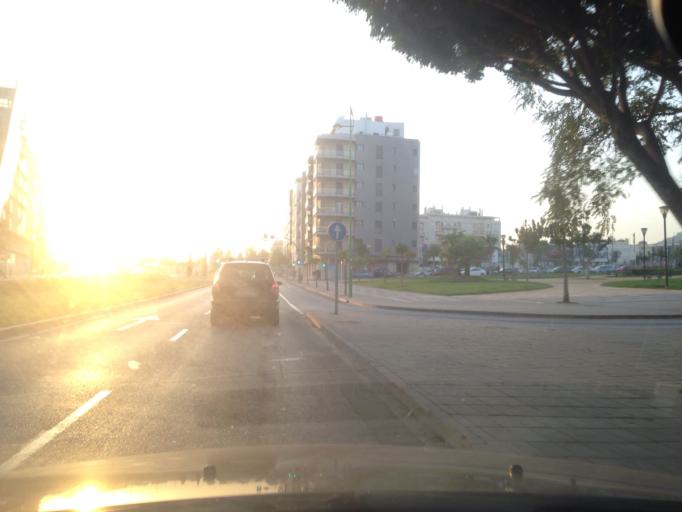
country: ES
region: Andalusia
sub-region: Provincia de Malaga
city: Malaga
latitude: 36.7200
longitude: -4.4609
